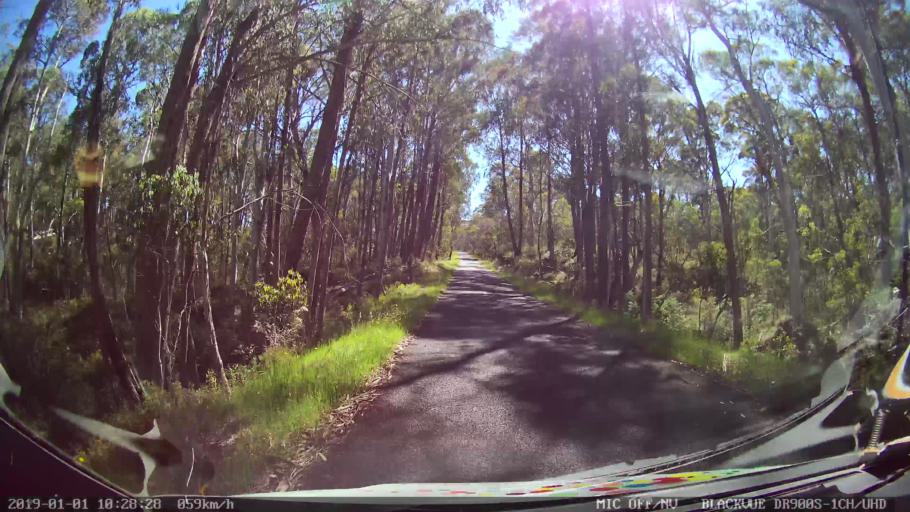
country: AU
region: New South Wales
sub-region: Snowy River
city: Jindabyne
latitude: -36.0600
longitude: 148.2407
